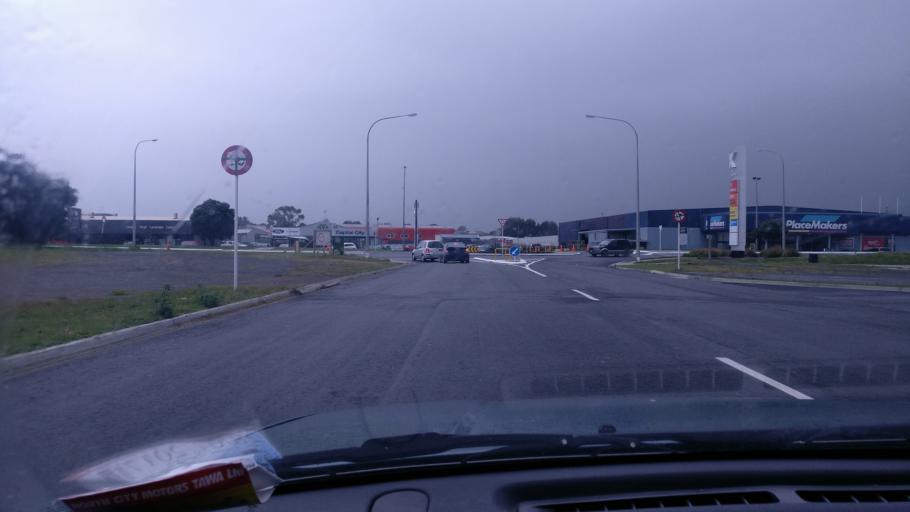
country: NZ
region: Wellington
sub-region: Kapiti Coast District
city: Paraparaumu
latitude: -40.9043
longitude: 174.9942
